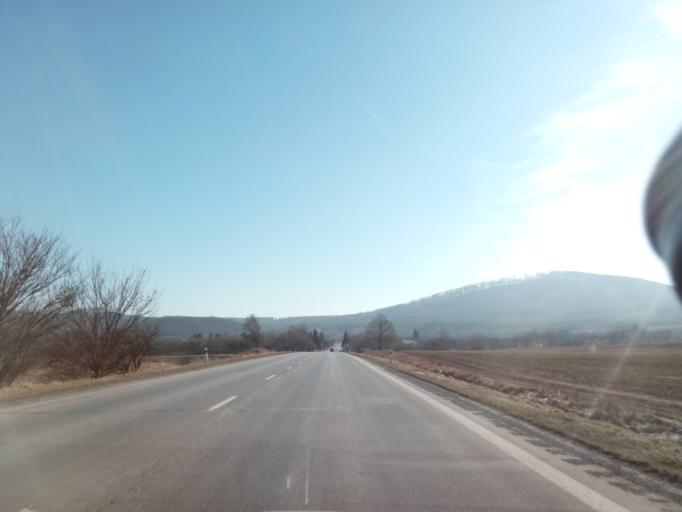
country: SK
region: Kosicky
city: Secovce
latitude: 48.7398
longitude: 21.4971
